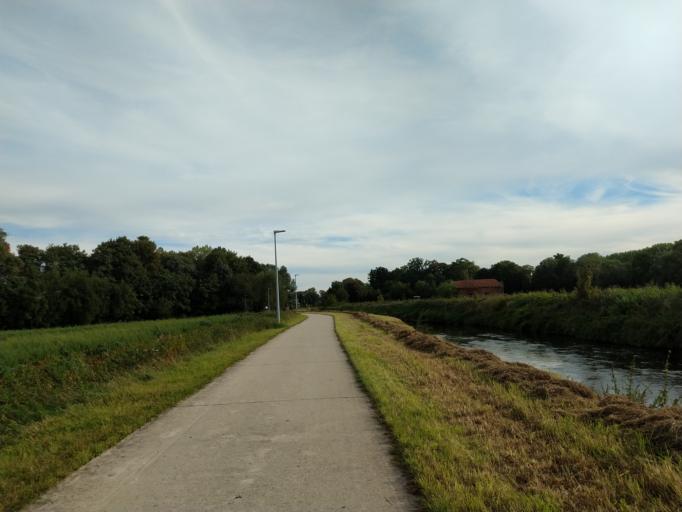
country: BE
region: Flanders
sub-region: Provincie Vlaams-Brabant
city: Leuven
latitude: 50.9151
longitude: 4.7091
